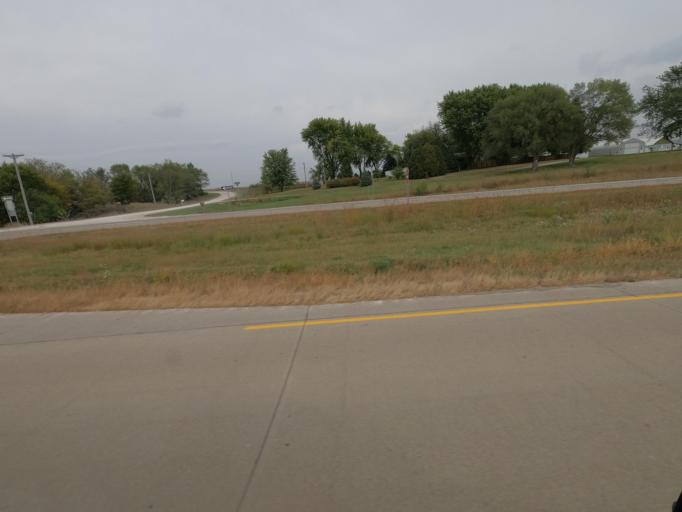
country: US
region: Iowa
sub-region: Mahaska County
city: Oskaloosa
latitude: 41.3376
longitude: -92.7329
